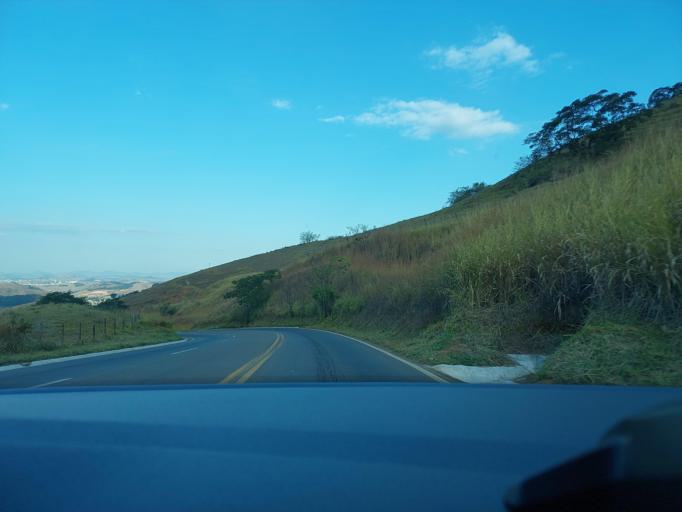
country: BR
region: Minas Gerais
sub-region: Muriae
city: Muriae
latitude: -21.0882
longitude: -42.4855
